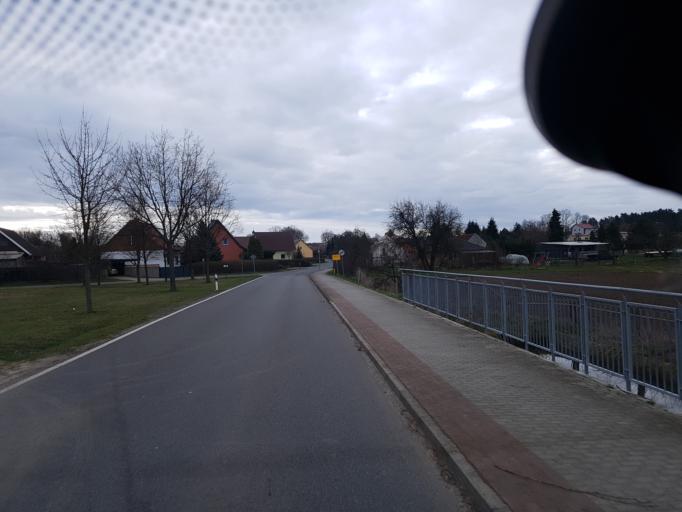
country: DE
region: Brandenburg
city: Gross Lindow
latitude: 52.1473
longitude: 14.5269
